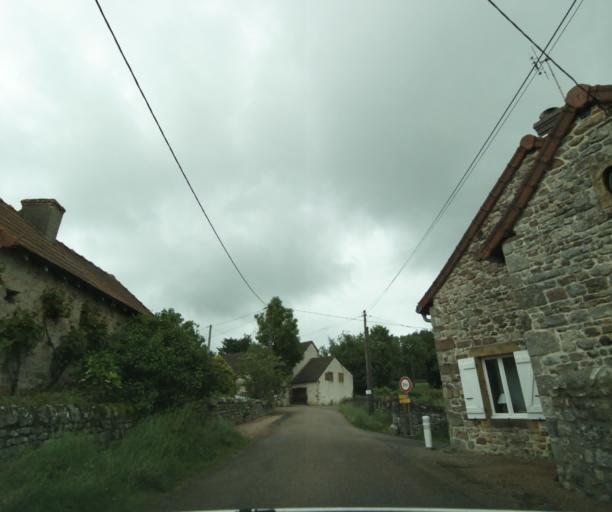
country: FR
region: Bourgogne
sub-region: Departement de Saone-et-Loire
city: Charolles
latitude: 46.4616
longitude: 4.3810
